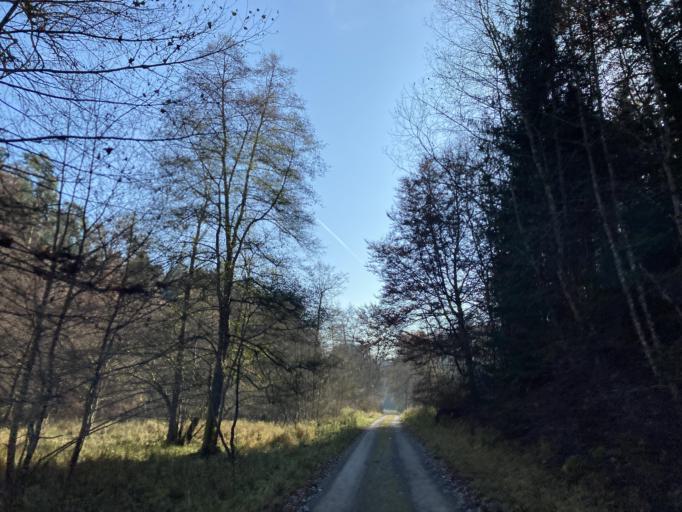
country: DE
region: Baden-Wuerttemberg
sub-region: Regierungsbezirk Stuttgart
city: Altdorf
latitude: 48.5855
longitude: 9.0137
